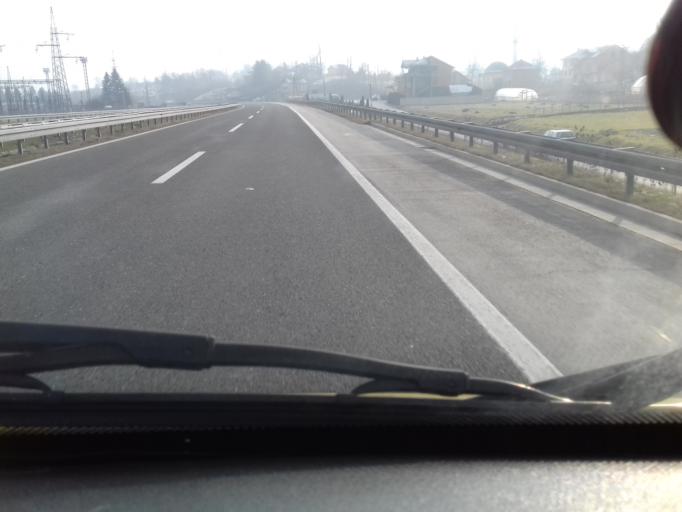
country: BA
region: Federation of Bosnia and Herzegovina
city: Dobrinje
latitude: 44.0389
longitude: 18.1217
